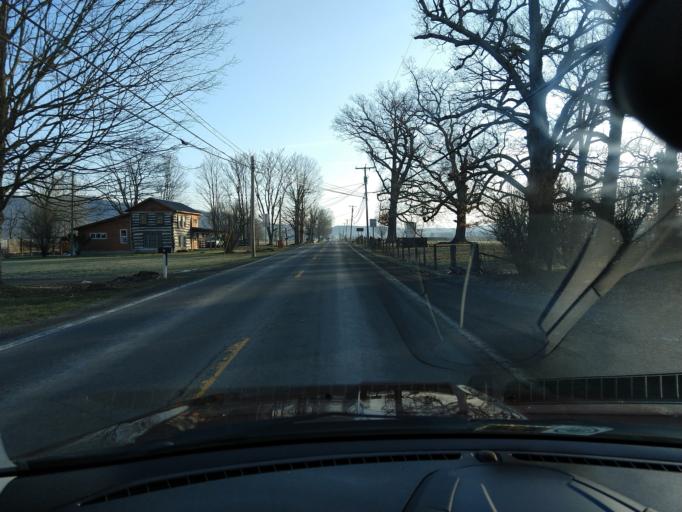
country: US
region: West Virginia
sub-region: Pocahontas County
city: Marlinton
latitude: 38.1391
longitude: -80.2070
